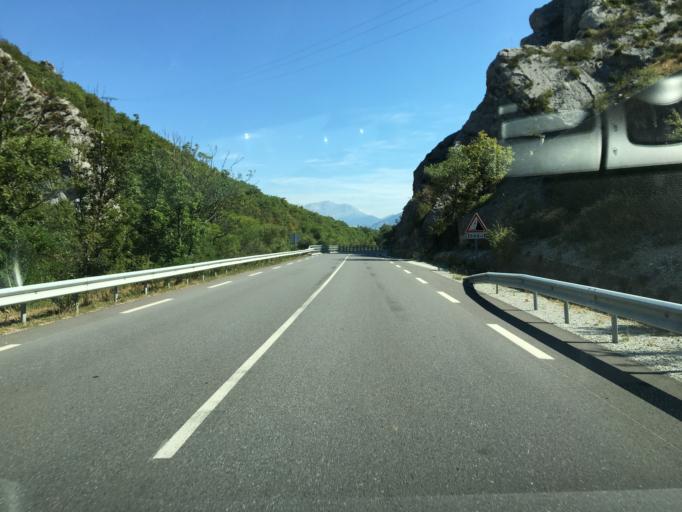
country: FR
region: Provence-Alpes-Cote d'Azur
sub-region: Departement des Hautes-Alpes
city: Serres
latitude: 44.4433
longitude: 5.7159
